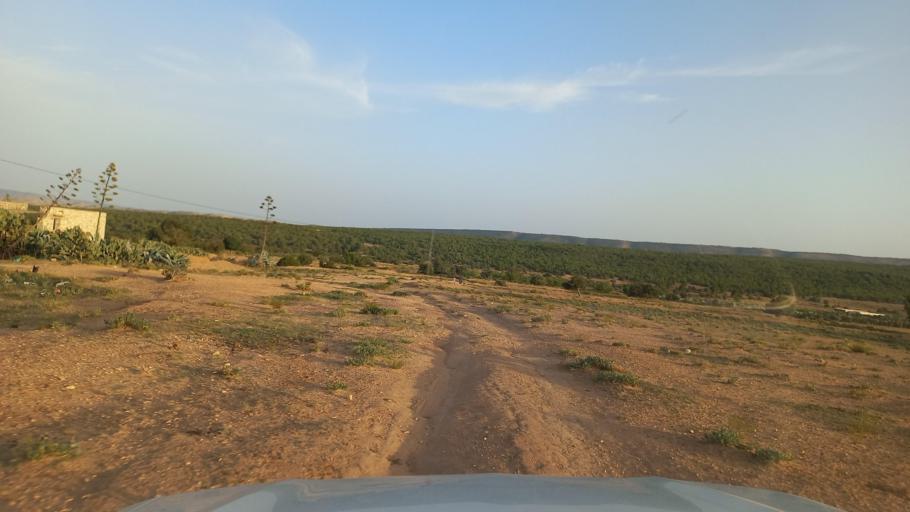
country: TN
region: Al Qasrayn
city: Sbiba
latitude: 35.4133
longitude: 8.9111
